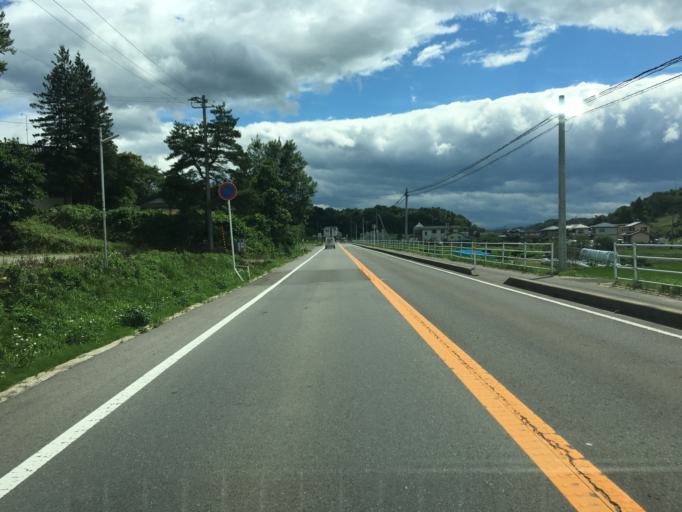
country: JP
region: Fukushima
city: Fukushima-shi
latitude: 37.6694
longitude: 140.5566
